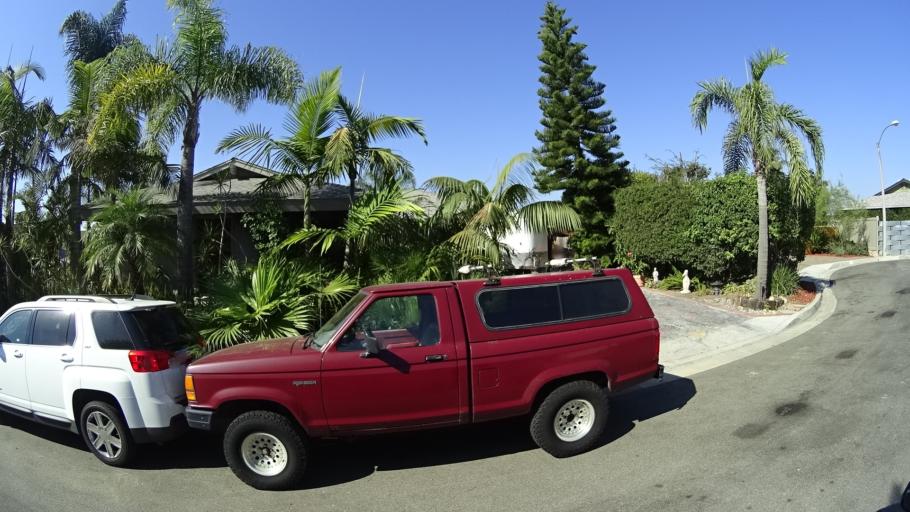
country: US
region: California
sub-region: Orange County
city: San Clemente
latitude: 33.4334
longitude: -117.6073
